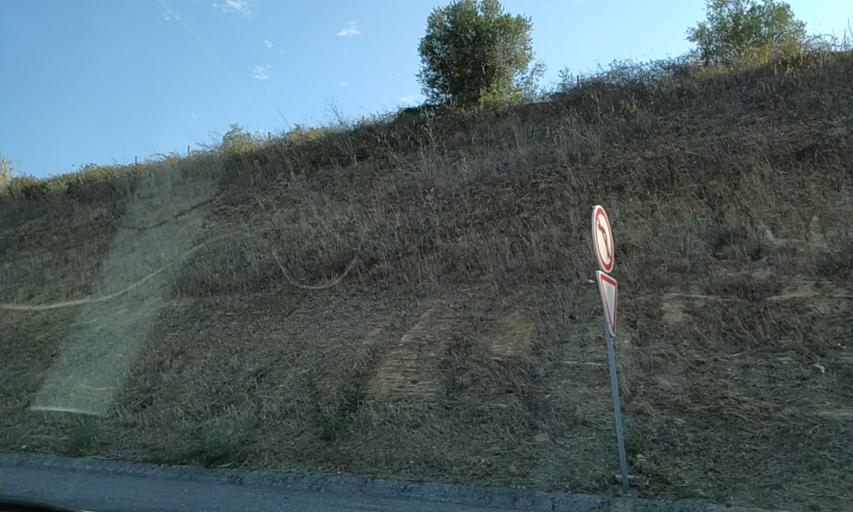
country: PT
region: Santarem
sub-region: Santarem
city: Santarem
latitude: 39.2232
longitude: -8.6966
